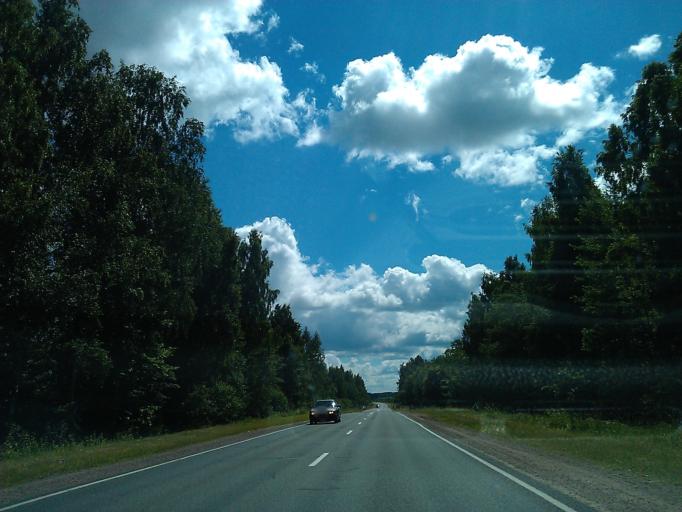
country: LV
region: Varaklani
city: Varaklani
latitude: 56.6074
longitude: 26.8460
